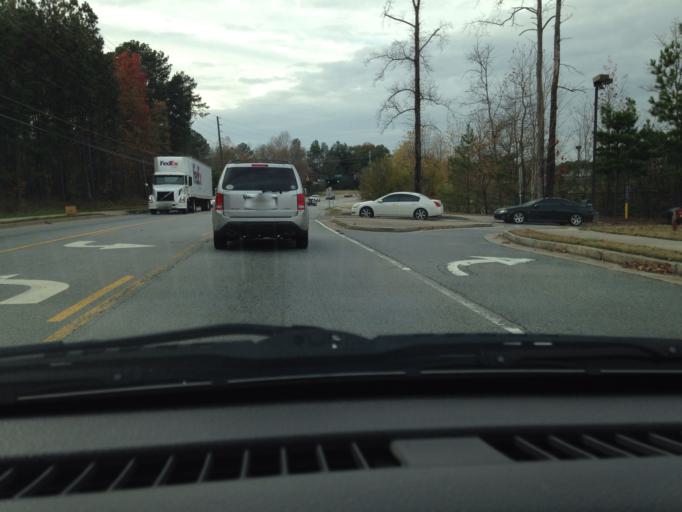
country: US
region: Georgia
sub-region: Fulton County
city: Johns Creek
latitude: 34.0902
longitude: -84.2038
